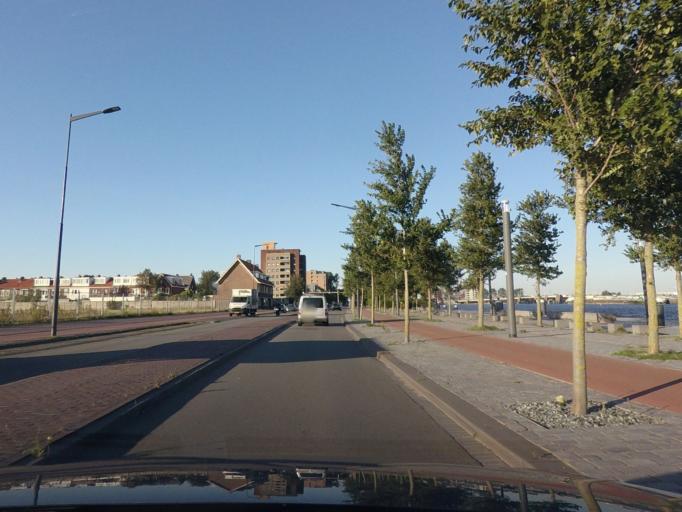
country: NL
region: North Holland
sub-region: Gemeente Haarlem
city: Haarlem
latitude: 52.3983
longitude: 4.6513
